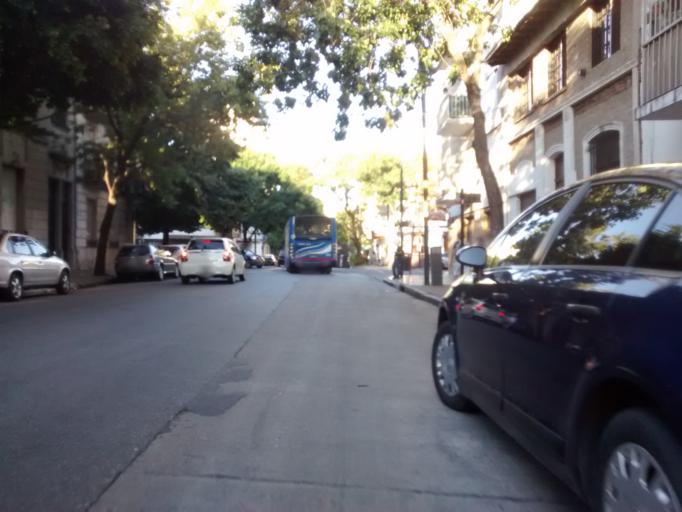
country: AR
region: Buenos Aires F.D.
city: Villa Santa Rita
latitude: -34.6100
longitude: -58.4471
